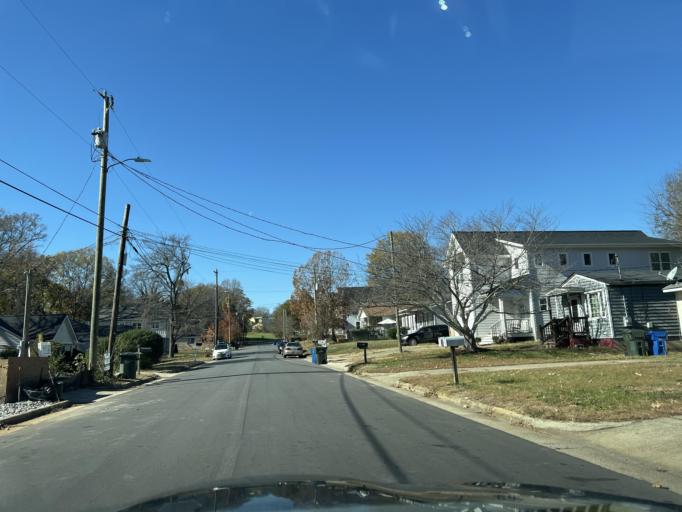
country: US
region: North Carolina
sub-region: Wake County
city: Raleigh
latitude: 35.7706
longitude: -78.6165
